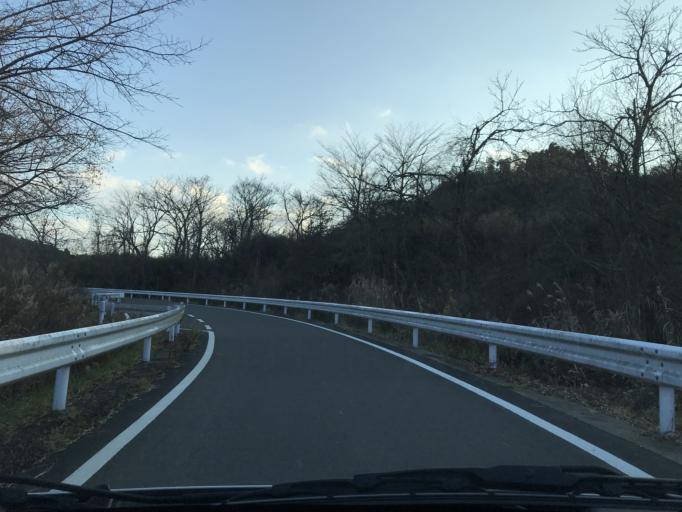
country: JP
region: Miyagi
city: Wakuya
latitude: 38.6879
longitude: 141.1064
